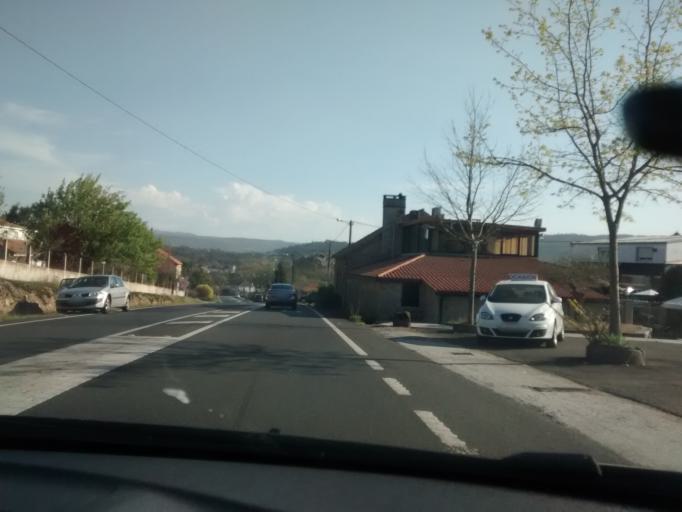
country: ES
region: Galicia
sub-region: Provincia da Coruna
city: Teo
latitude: 42.7696
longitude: -8.5499
